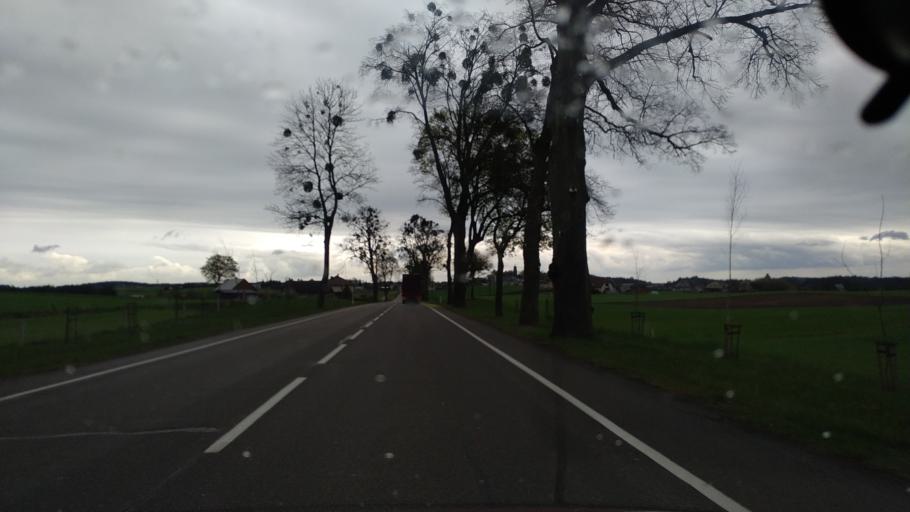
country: PL
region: Pomeranian Voivodeship
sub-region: Powiat starogardzki
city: Kaliska
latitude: 53.8855
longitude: 18.2032
